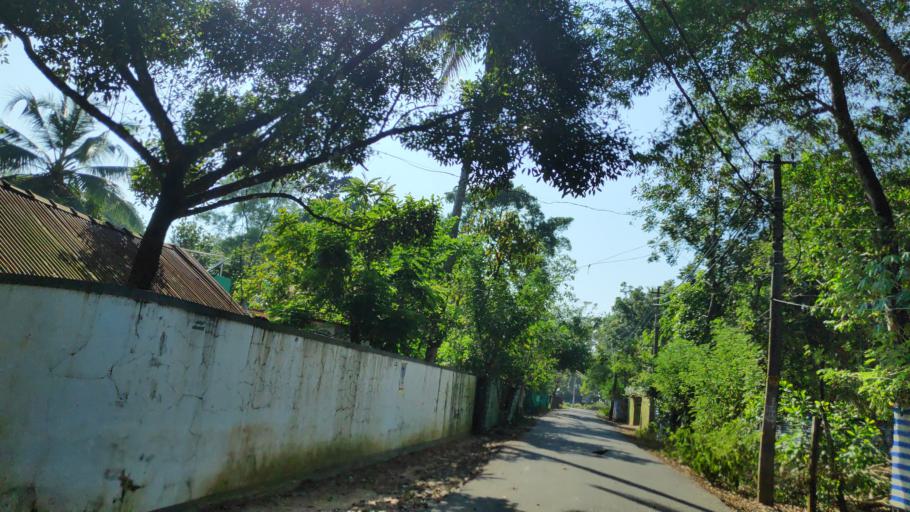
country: IN
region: Kerala
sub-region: Alappuzha
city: Alleppey
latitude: 9.5331
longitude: 76.3111
